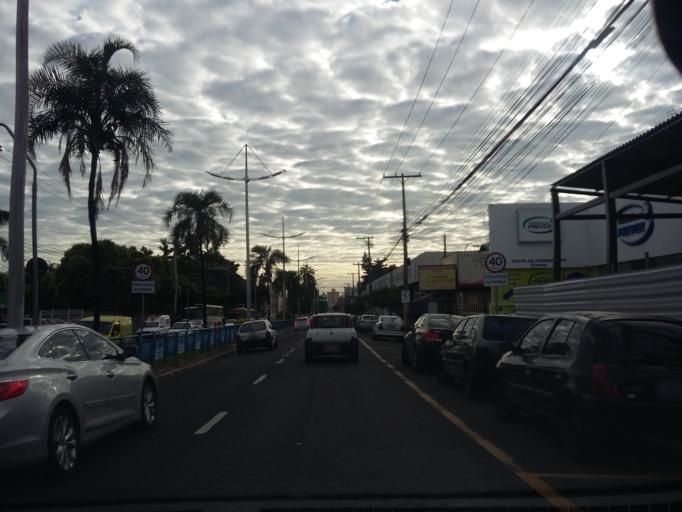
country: BR
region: Sao Paulo
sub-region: Sao Jose Do Rio Preto
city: Sao Jose do Rio Preto
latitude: -20.8294
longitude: -49.3971
